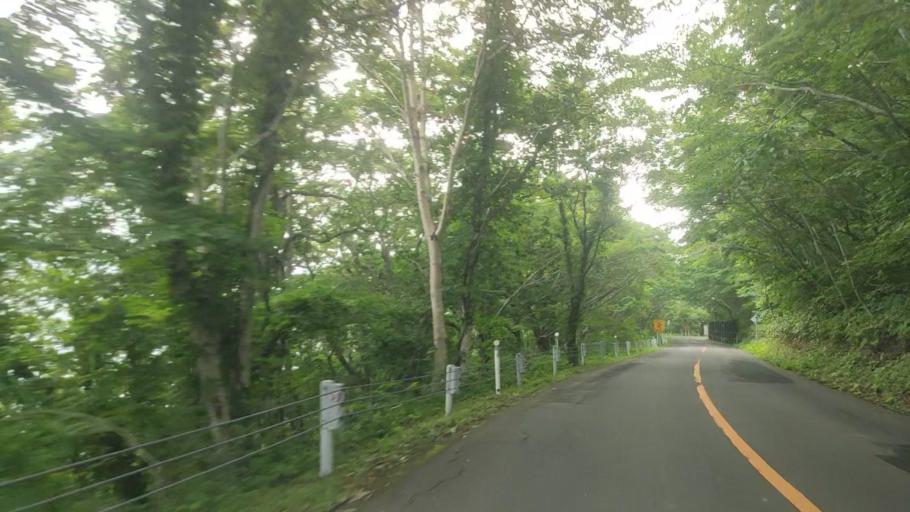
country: JP
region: Hokkaido
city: Hakodate
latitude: 41.7602
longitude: 140.7030
